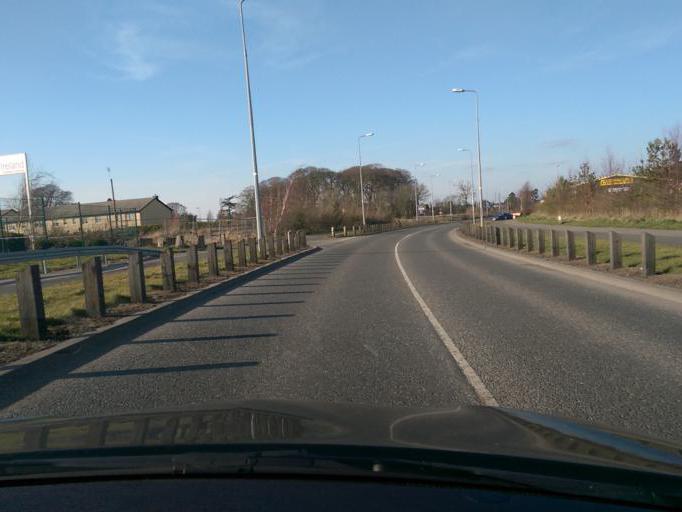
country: IE
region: Leinster
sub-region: Kildare
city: Naas
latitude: 53.2111
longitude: -6.6806
